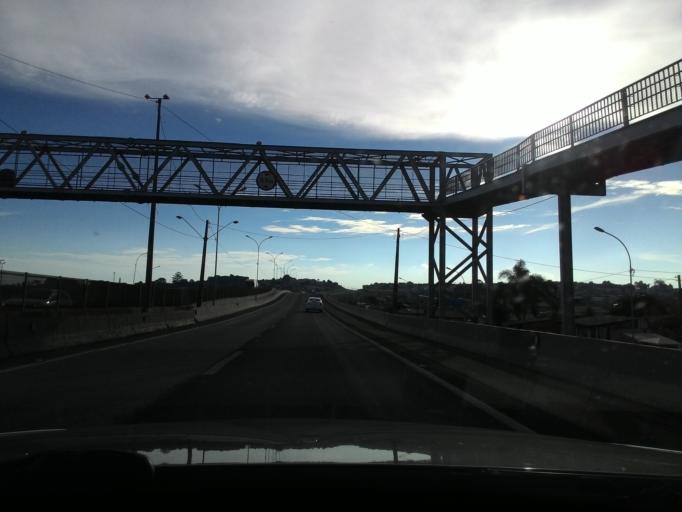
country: BR
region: Parana
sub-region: Pinhais
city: Pinhais
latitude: -25.3838
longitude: -49.1691
